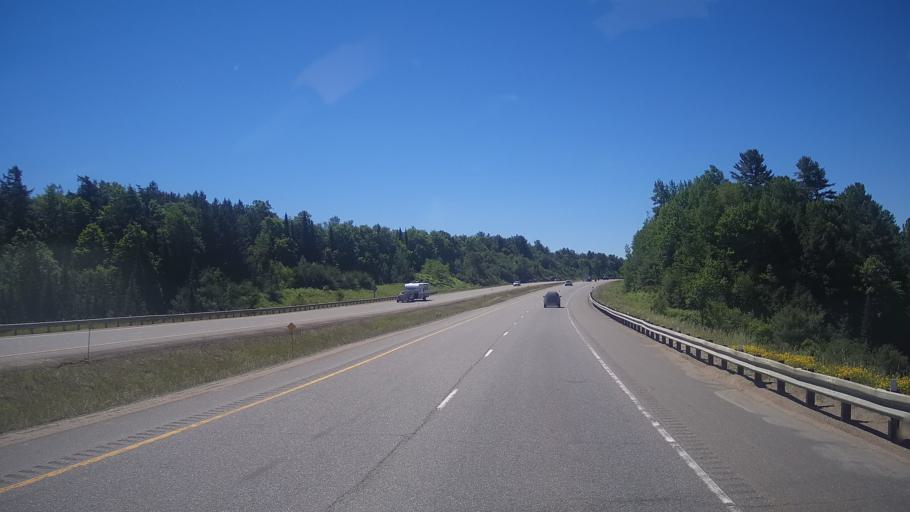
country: CA
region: Ontario
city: Bracebridge
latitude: 45.0287
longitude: -79.2924
